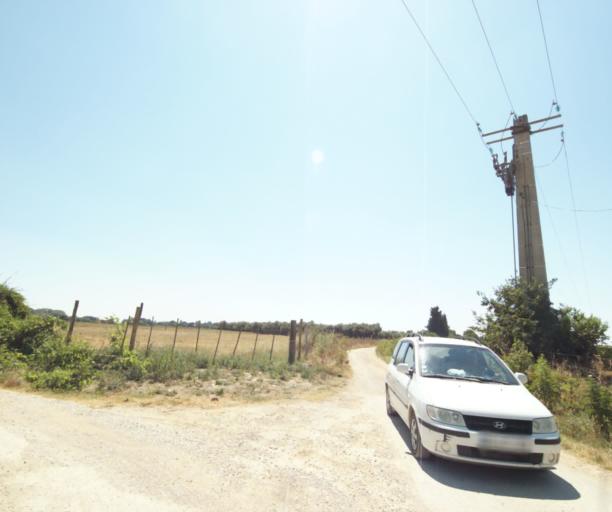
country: FR
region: Languedoc-Roussillon
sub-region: Departement de l'Herault
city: Marsillargues
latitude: 43.6557
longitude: 4.1849
